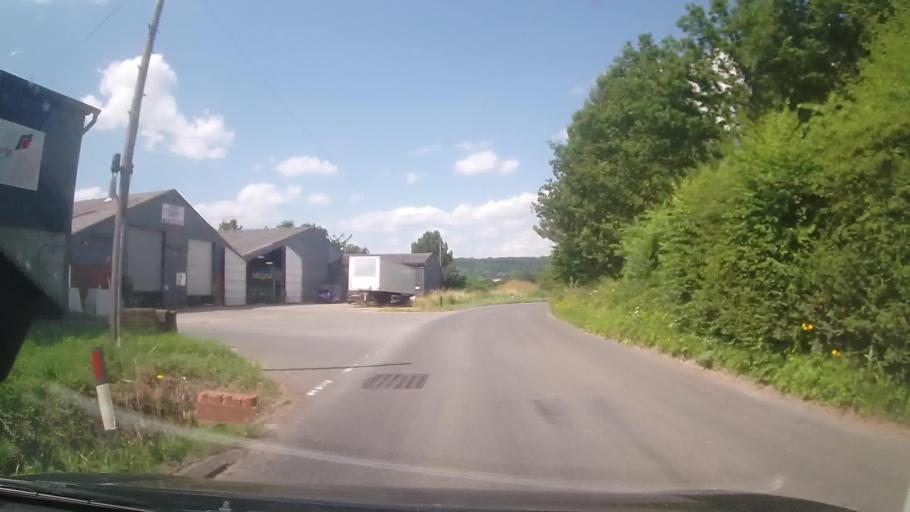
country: GB
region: England
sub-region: Herefordshire
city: Ocle Pychard
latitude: 52.0674
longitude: -2.5830
